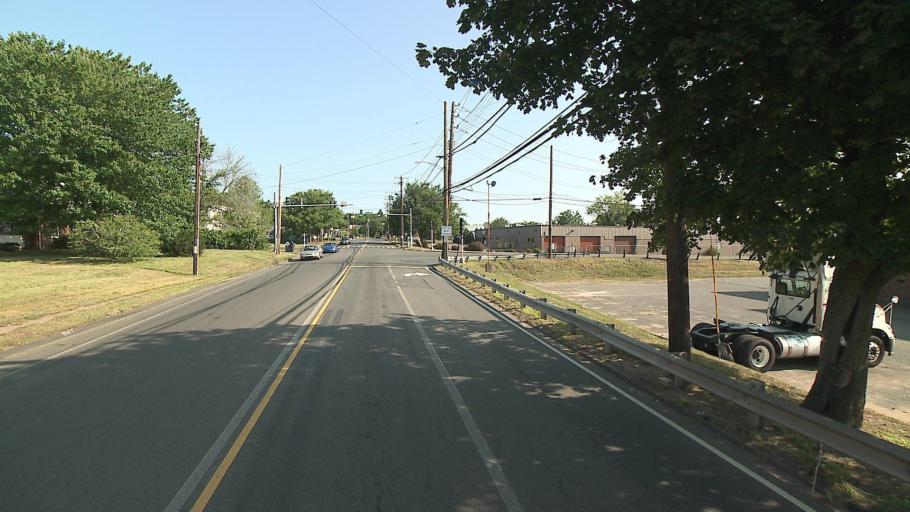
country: US
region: Connecticut
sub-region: New Haven County
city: Hamden
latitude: 41.3683
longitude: -72.8867
